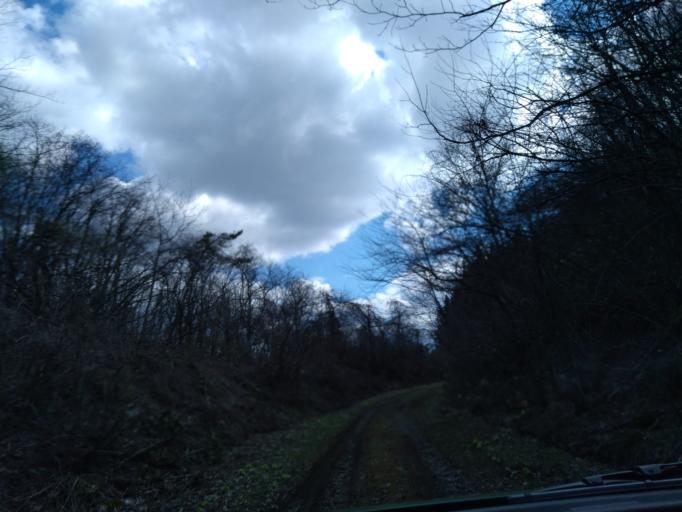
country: JP
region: Iwate
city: Ichinoseki
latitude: 38.9827
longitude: 141.0188
